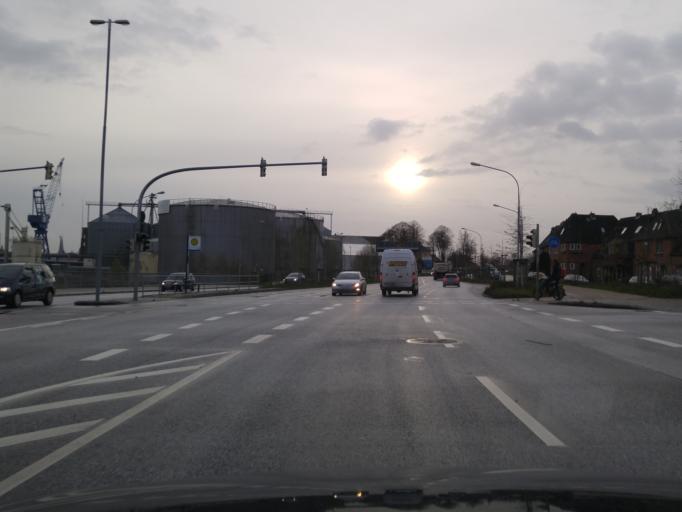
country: DE
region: Schleswig-Holstein
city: Luebeck
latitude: 53.8839
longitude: 10.6896
